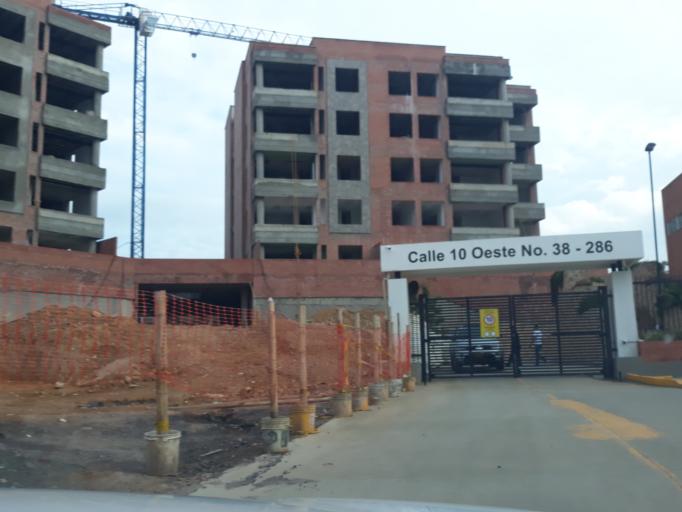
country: CO
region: Valle del Cauca
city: Cali
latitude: 3.4296
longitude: -76.5544
